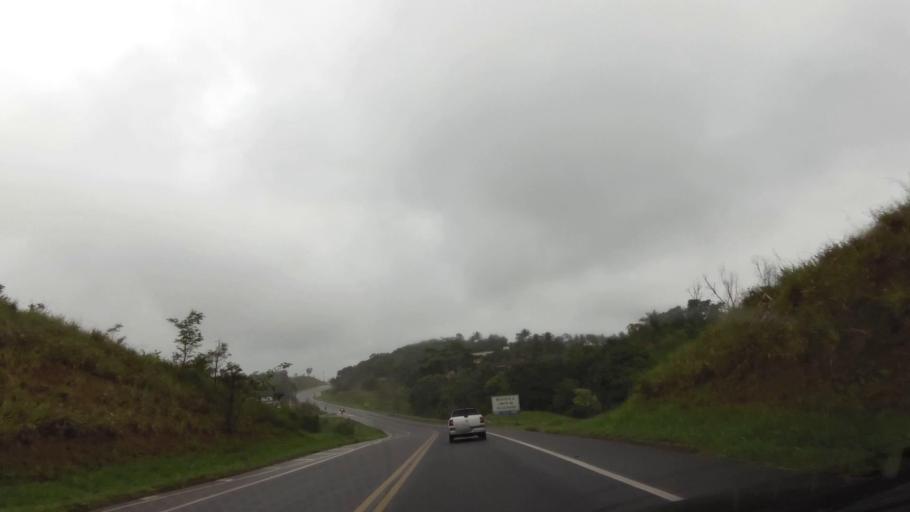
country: BR
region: Espirito Santo
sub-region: Guarapari
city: Guarapari
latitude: -20.7354
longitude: -40.5538
